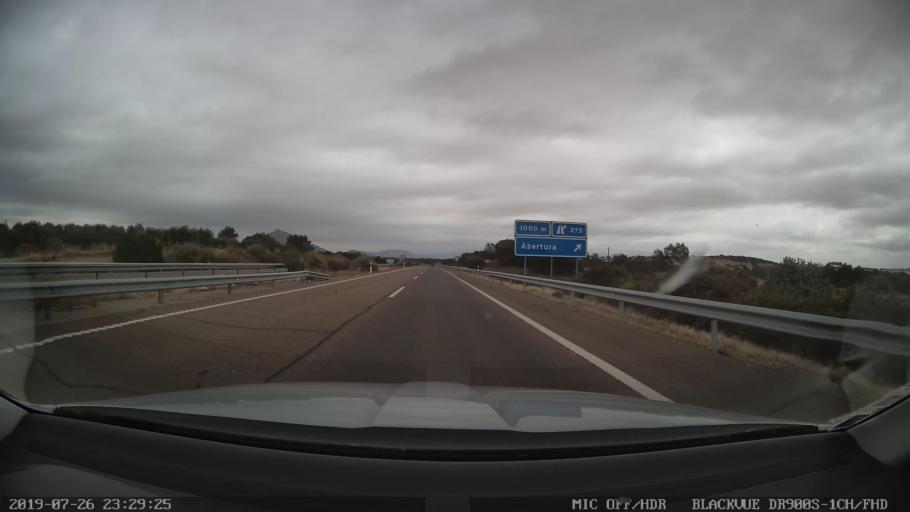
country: ES
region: Extremadura
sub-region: Provincia de Caceres
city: Villamesias
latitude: 39.2598
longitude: -5.8622
